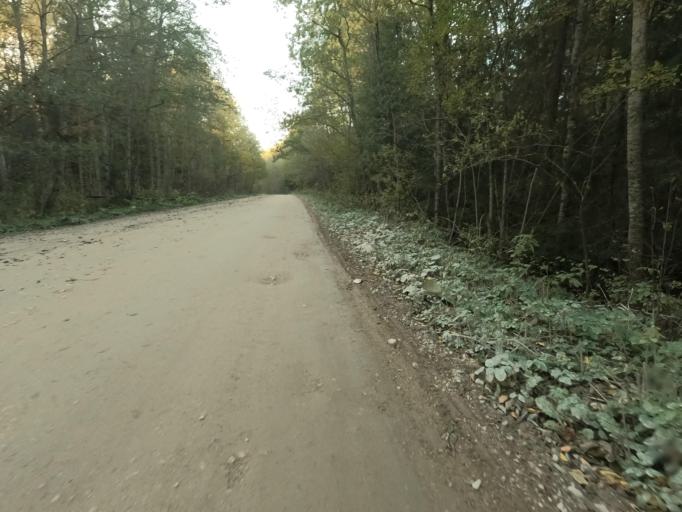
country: RU
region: Leningrad
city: Lyuban'
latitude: 59.0047
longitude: 31.0956
